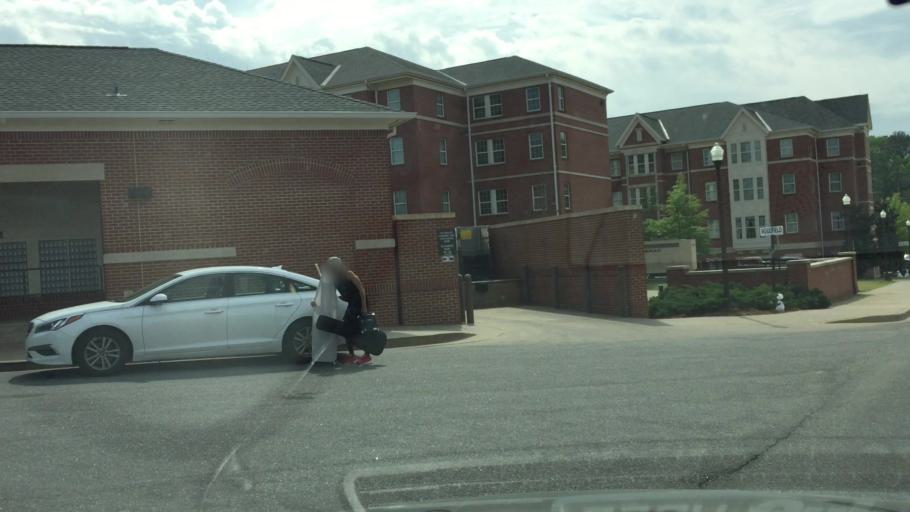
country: US
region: Alabama
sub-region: Lee County
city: Auburn
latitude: 32.6049
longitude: -85.4939
